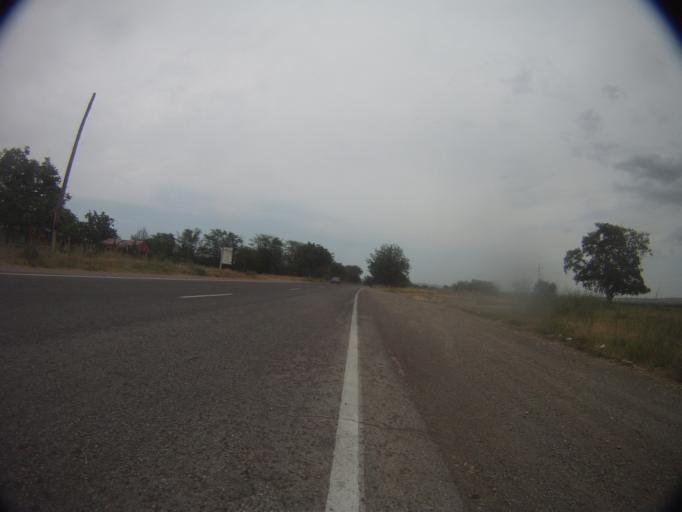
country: GE
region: Kakheti
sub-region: Gurjaani
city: Gurjaani
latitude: 41.6412
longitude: 45.6498
